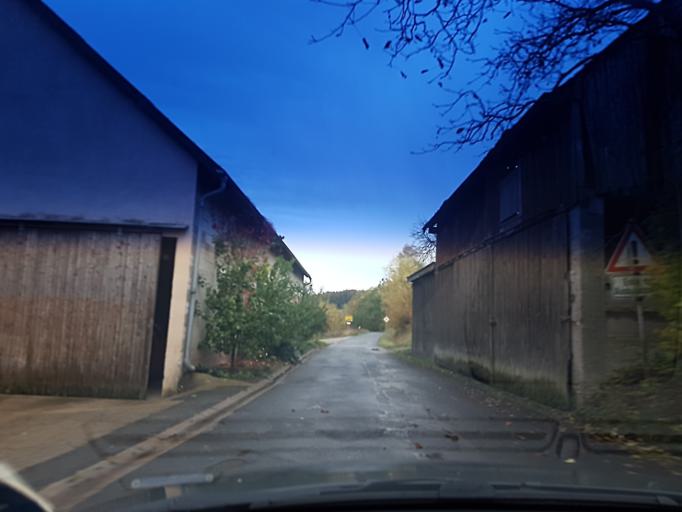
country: DE
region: Bavaria
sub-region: Regierungsbezirk Unterfranken
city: Geiselwind
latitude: 49.7573
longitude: 10.5239
